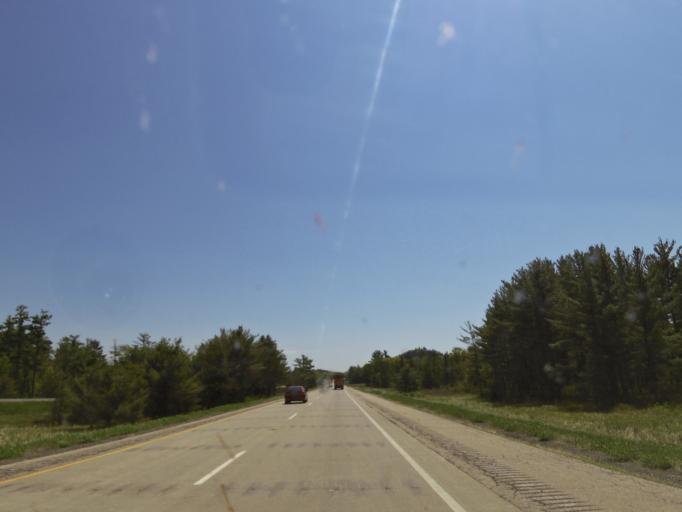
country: US
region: Wisconsin
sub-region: Monroe County
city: Tomah
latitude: 44.1699
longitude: -90.5915
